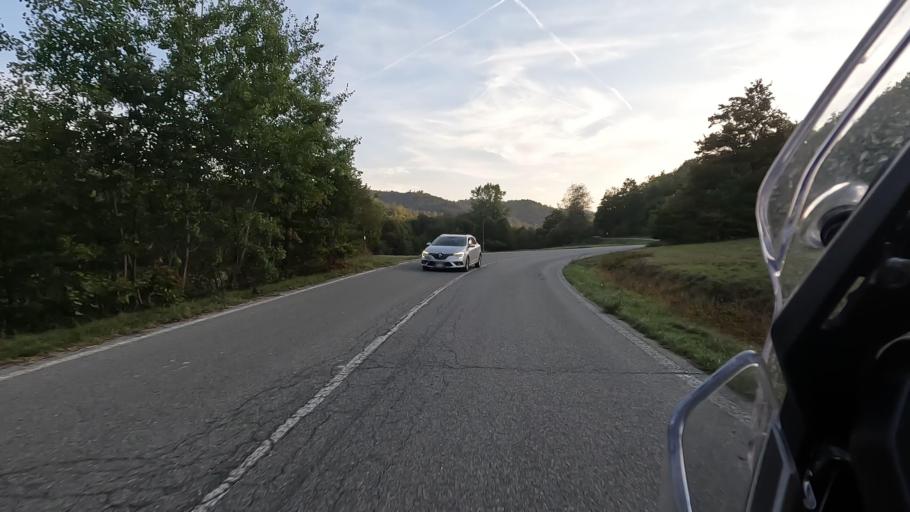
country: IT
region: Liguria
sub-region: Provincia di Savona
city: Mioglia
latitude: 44.5061
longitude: 8.4355
